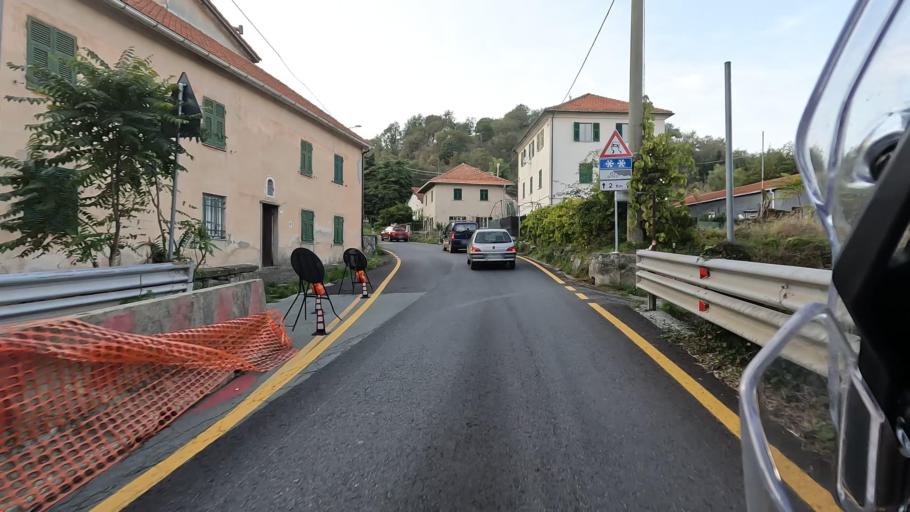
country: IT
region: Liguria
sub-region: Provincia di Savona
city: Osteria dei Cacciatori-Stella
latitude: 44.4183
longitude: 8.4799
